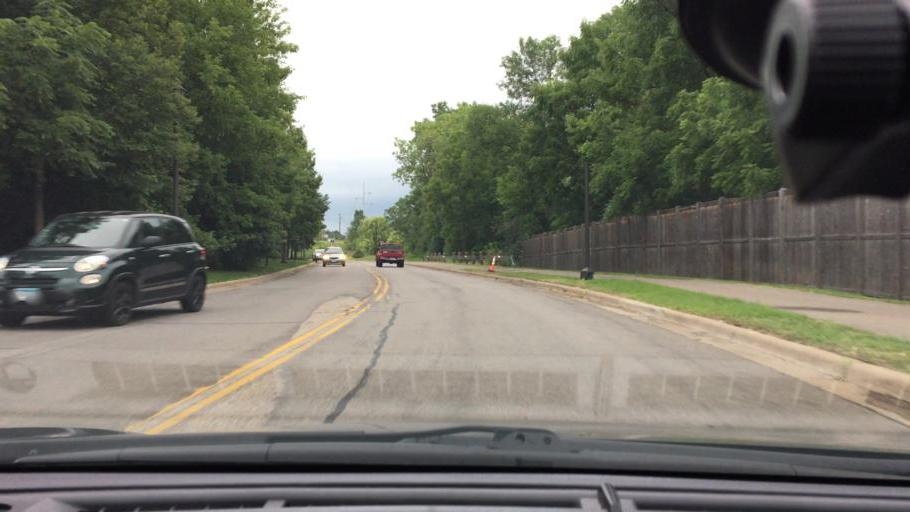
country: US
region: Minnesota
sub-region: Hennepin County
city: Saint Louis Park
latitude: 44.9775
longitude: -93.3518
